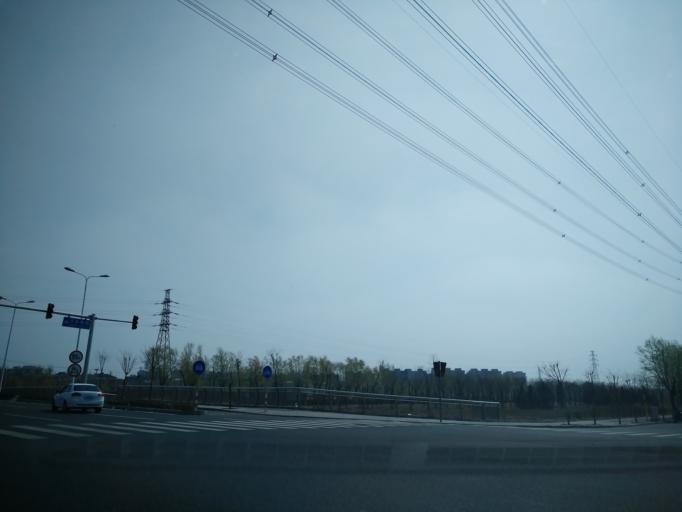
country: CN
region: Beijing
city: Qingyundian
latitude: 39.7530
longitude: 116.5292
